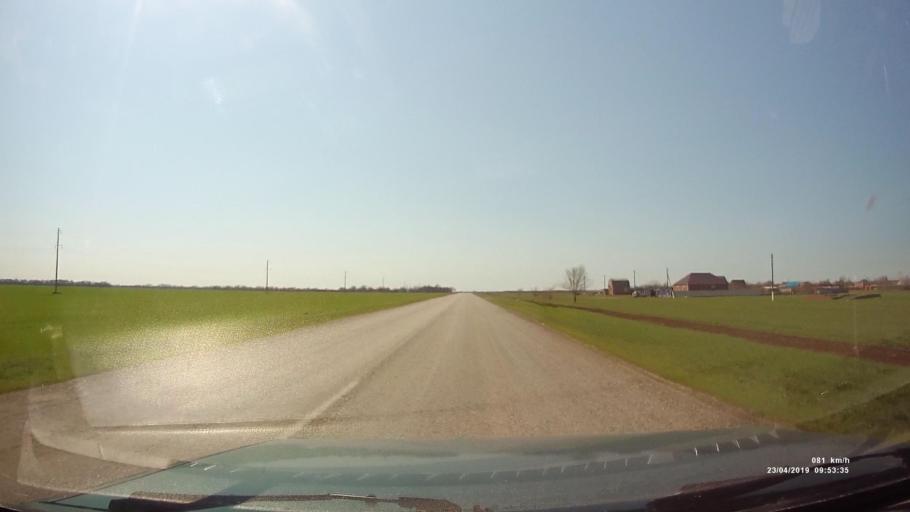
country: RU
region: Rostov
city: Orlovskiy
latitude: 46.8311
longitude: 42.0509
